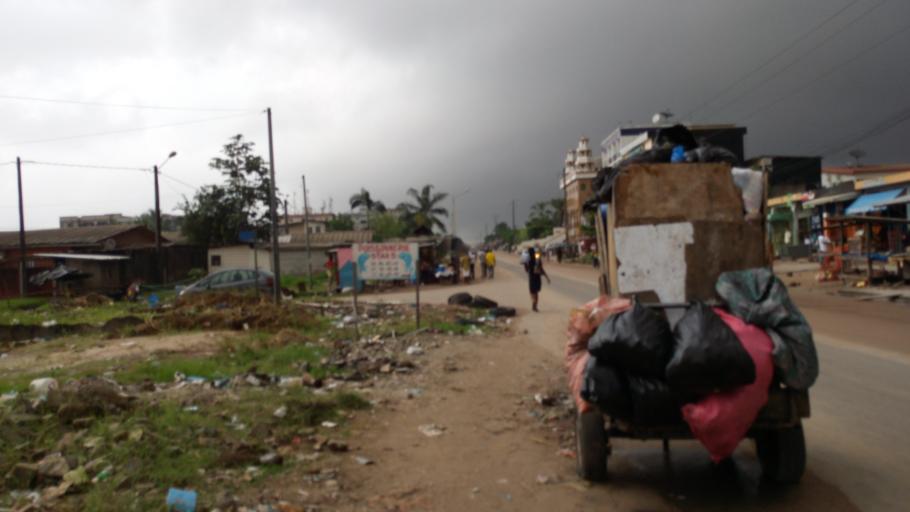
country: CI
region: Lagunes
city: Abobo
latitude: 5.4049
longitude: -3.9948
